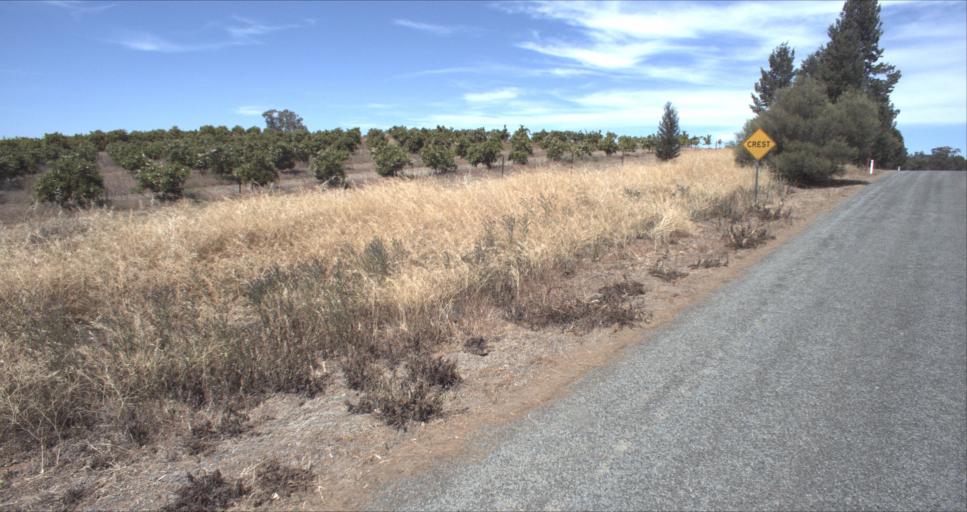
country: AU
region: New South Wales
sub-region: Leeton
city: Leeton
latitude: -34.6670
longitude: 146.4469
